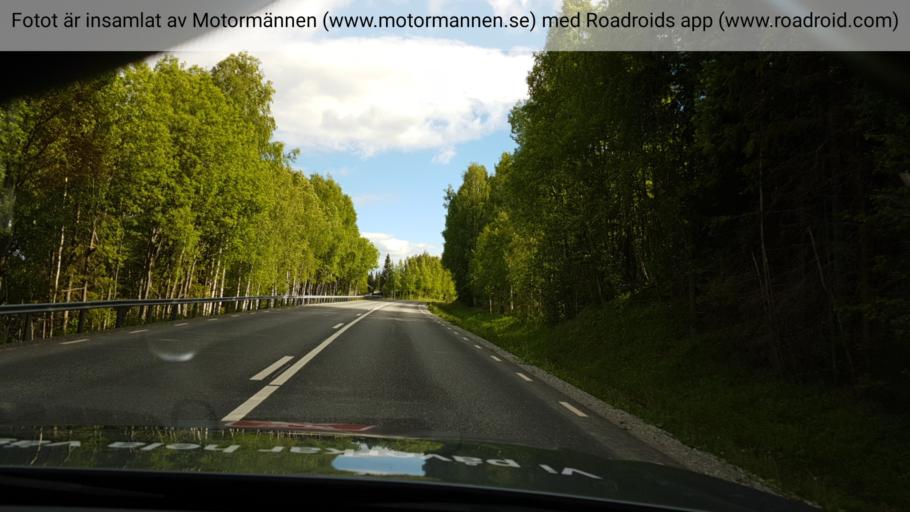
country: SE
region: Jaemtland
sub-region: Stroemsunds Kommun
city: Stroemsund
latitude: 64.1667
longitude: 15.6736
